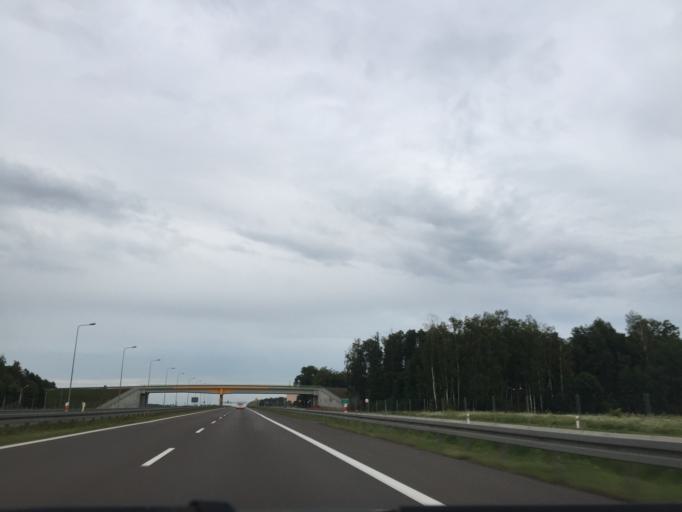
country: PL
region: Podlasie
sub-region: Powiat bialostocki
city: Tykocin
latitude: 53.1435
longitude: 22.7941
